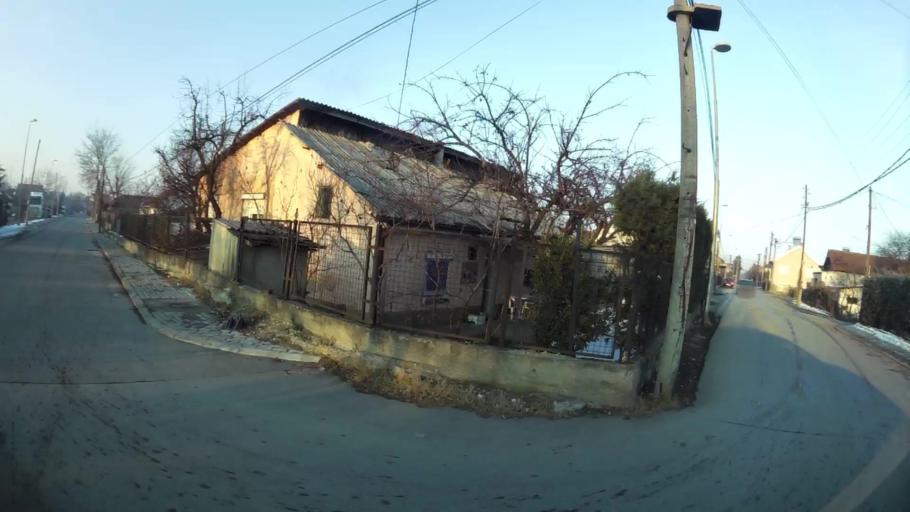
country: MK
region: Kisela Voda
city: Kisela Voda
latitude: 41.9738
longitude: 21.4875
